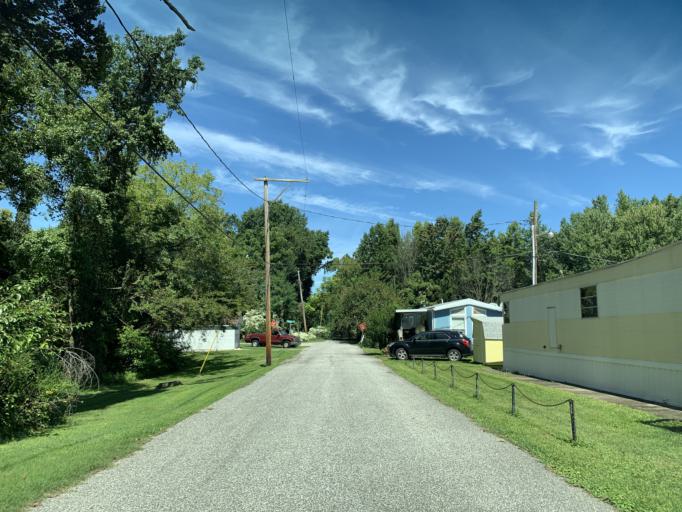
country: US
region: Maryland
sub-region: Baltimore County
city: Edgemere
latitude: 39.2238
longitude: -76.4362
